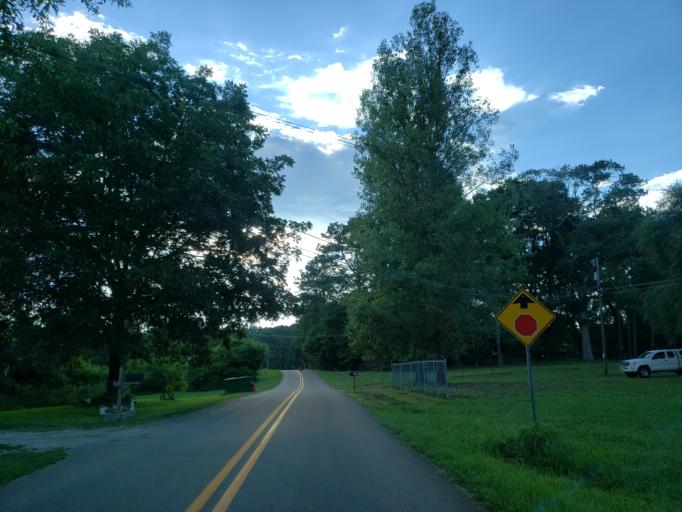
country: US
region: Georgia
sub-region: Cherokee County
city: Ball Ground
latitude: 34.3628
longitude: -84.4818
